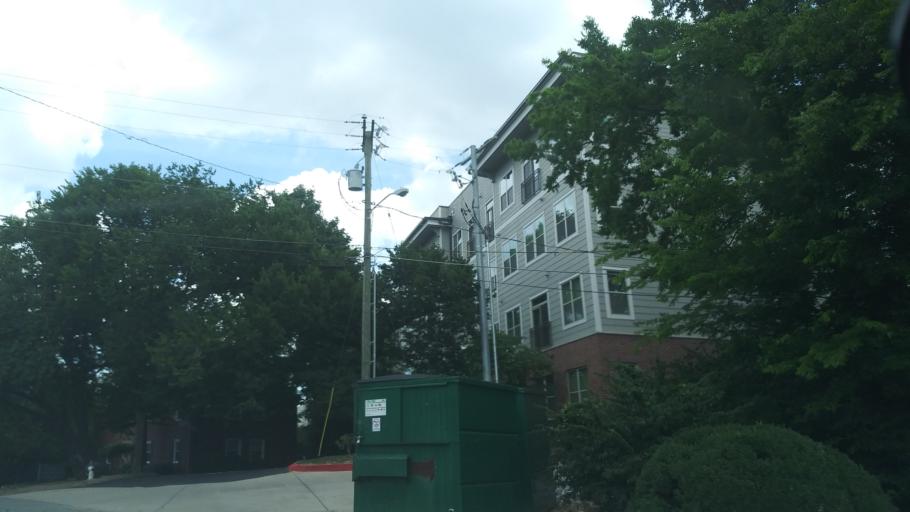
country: US
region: Tennessee
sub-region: Davidson County
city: Nashville
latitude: 36.1419
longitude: -86.8213
